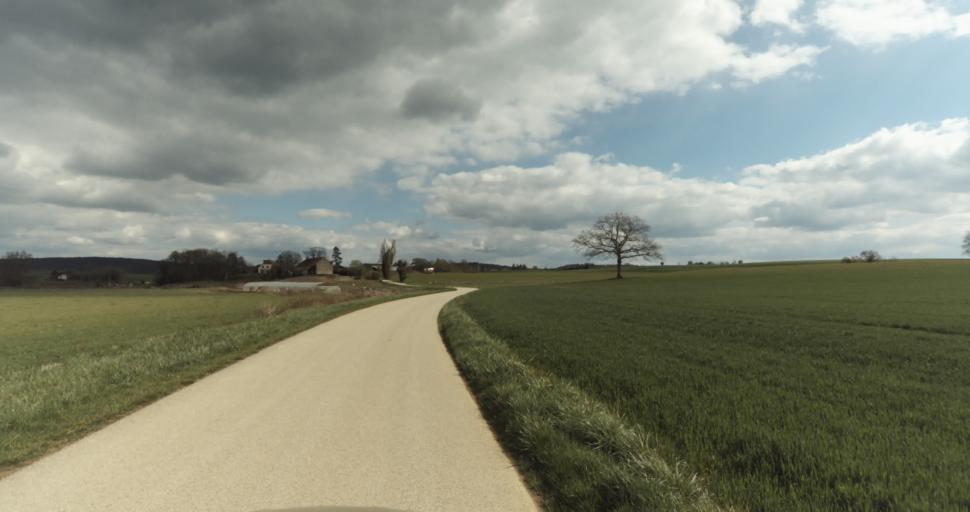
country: FR
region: Bourgogne
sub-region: Departement de la Cote-d'Or
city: Auxonne
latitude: 47.1793
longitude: 5.4653
